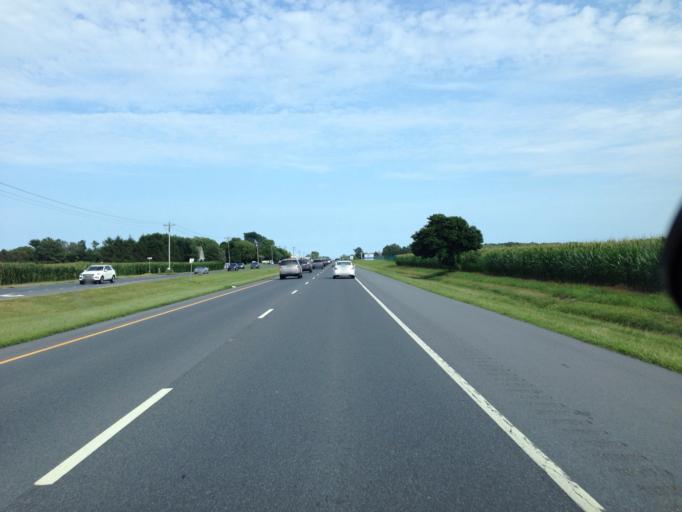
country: US
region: Delaware
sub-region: Sussex County
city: Milton
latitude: 38.7802
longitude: -75.2342
